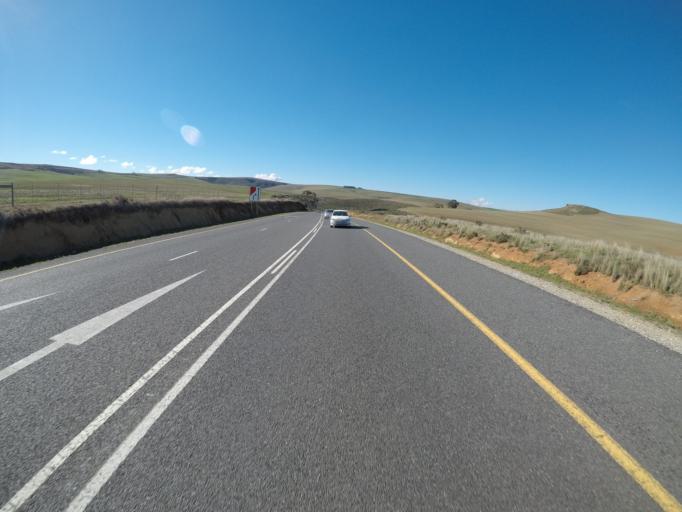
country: ZA
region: Western Cape
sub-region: Overberg District Municipality
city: Hermanus
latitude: -34.2334
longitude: 19.2357
